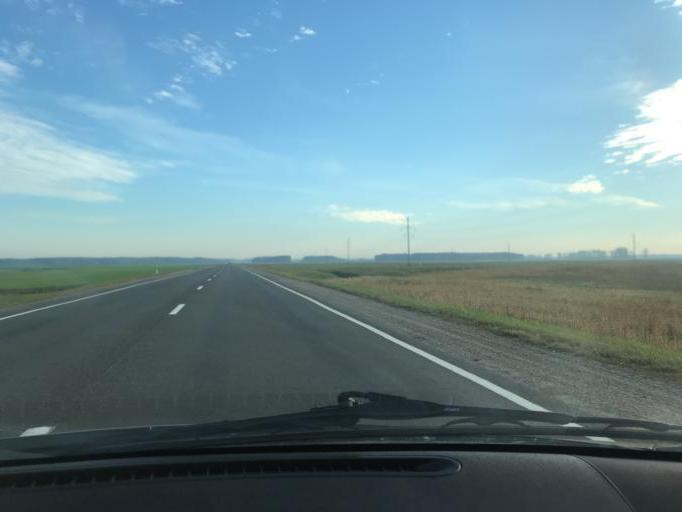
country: BY
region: Brest
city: Drahichyn
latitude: 52.2020
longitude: 25.0500
